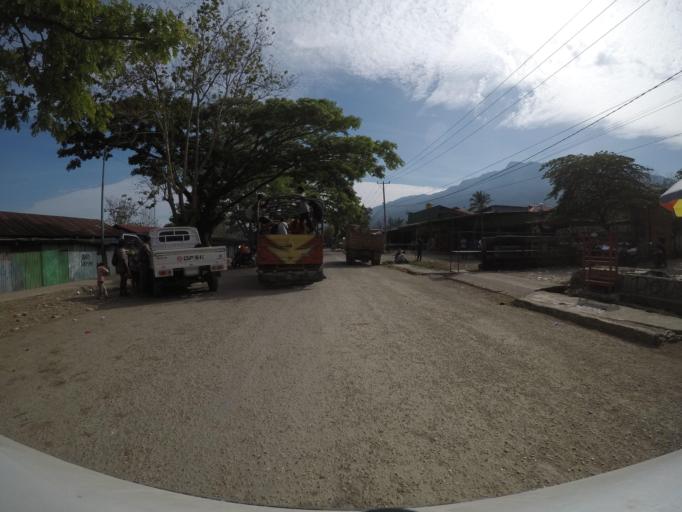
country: TL
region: Bobonaro
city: Maliana
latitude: -8.9893
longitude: 125.2211
